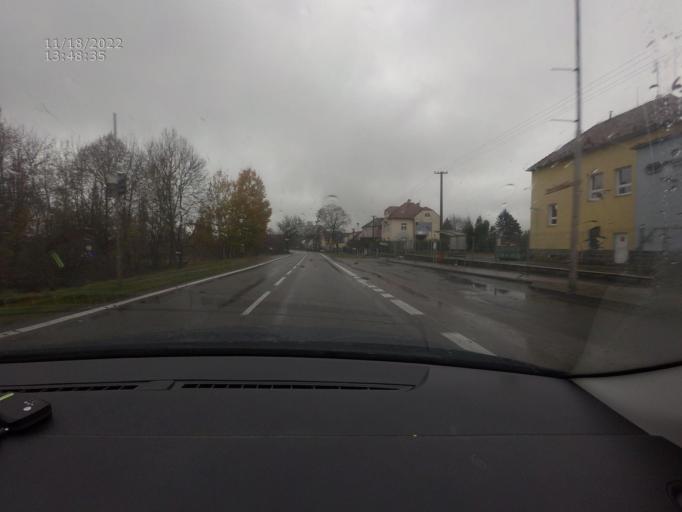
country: CZ
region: Jihocesky
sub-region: Okres Strakonice
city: Blatna
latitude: 49.4177
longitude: 13.8852
